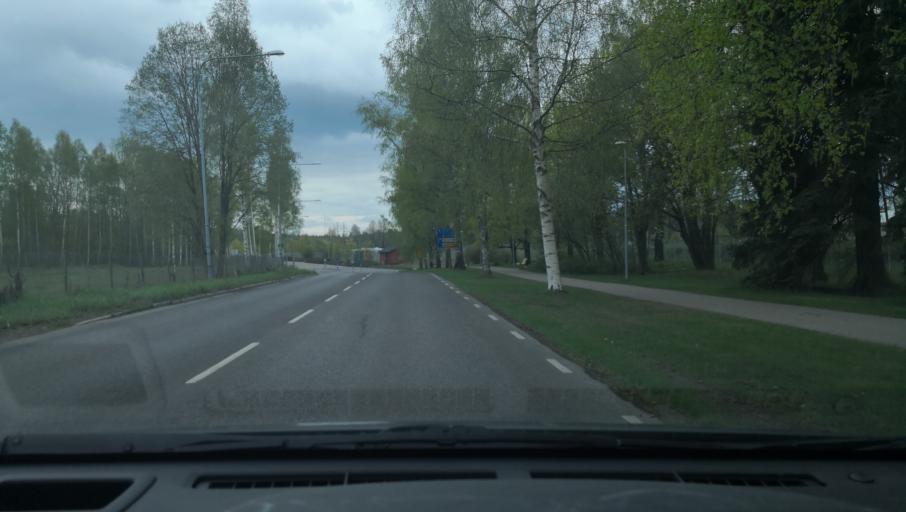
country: SE
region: Dalarna
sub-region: Avesta Kommun
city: Avesta
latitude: 60.1261
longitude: 16.2188
